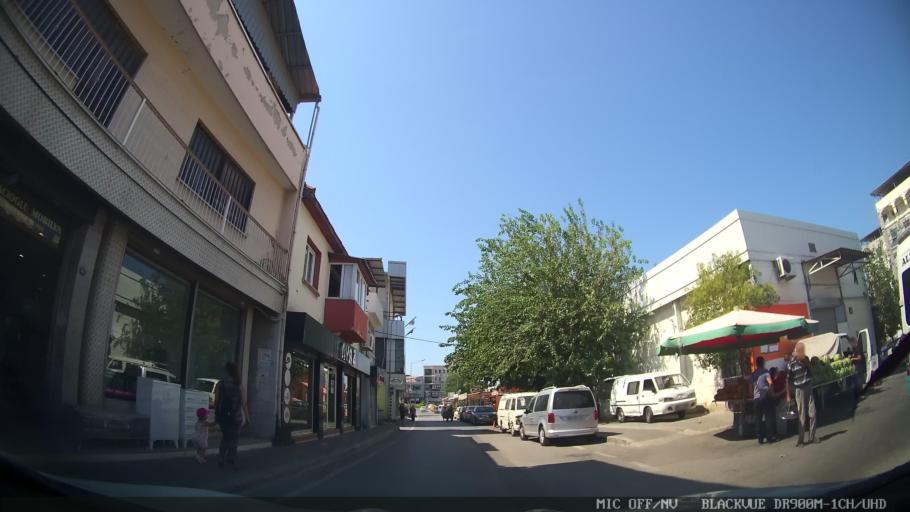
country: TR
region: Izmir
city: Karsiyaka
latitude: 38.4953
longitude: 27.0635
